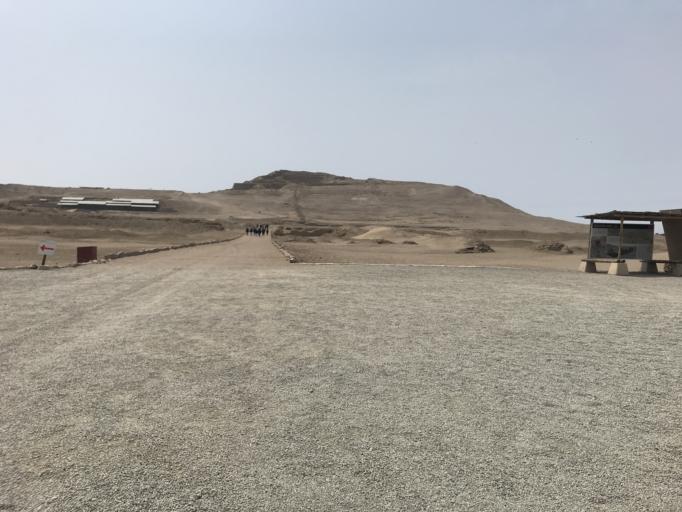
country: PE
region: Lima
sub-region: Lima
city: Punta Hermosa
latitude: -12.2572
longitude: -76.9037
